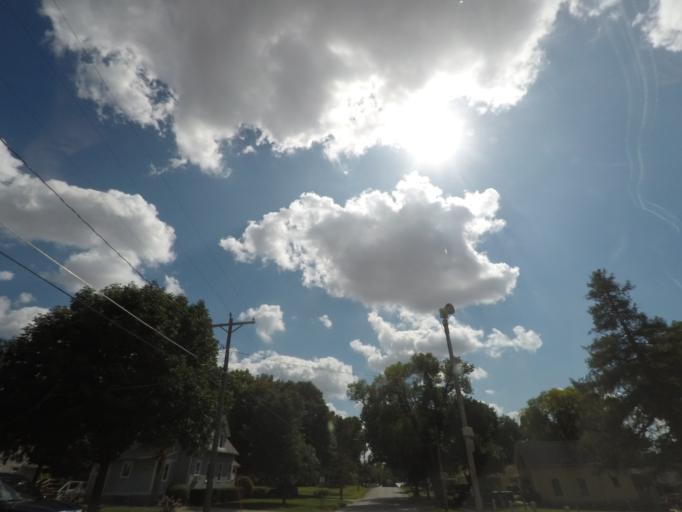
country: US
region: Iowa
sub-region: Story County
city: Nevada
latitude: 42.0213
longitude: -93.4591
